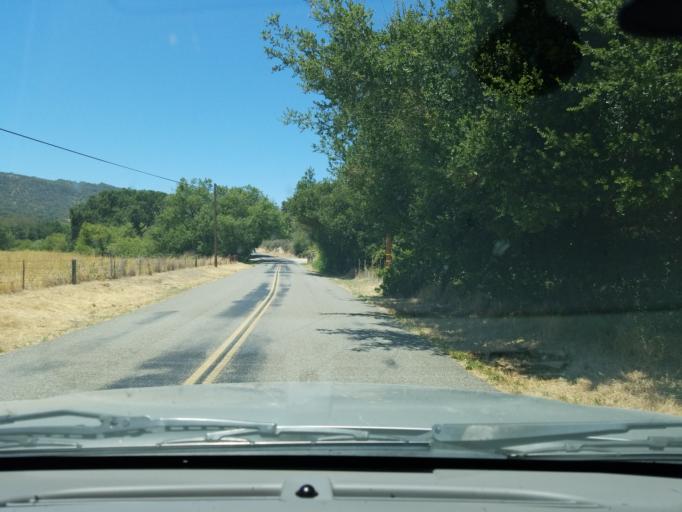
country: US
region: California
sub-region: Monterey County
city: Carmel Valley Village
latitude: 36.4431
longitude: -121.6566
